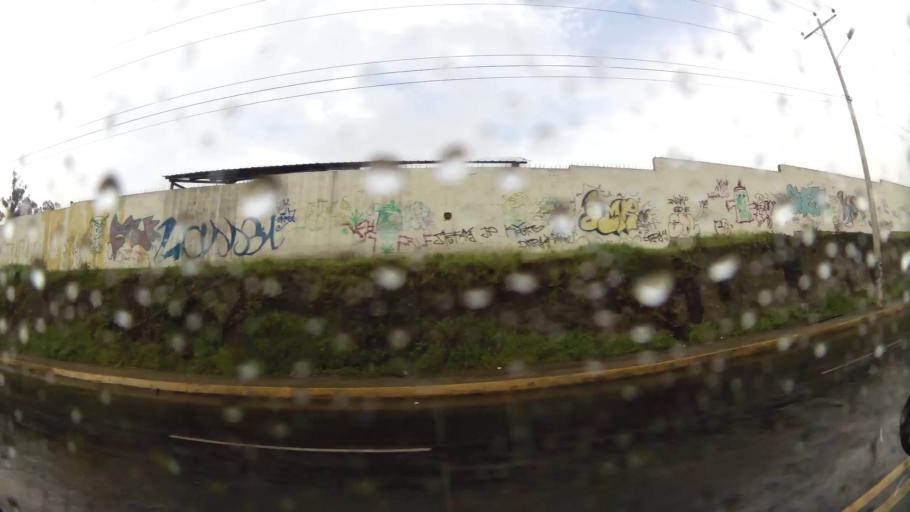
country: EC
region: Pichincha
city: Quito
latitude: -0.0978
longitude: -78.4975
